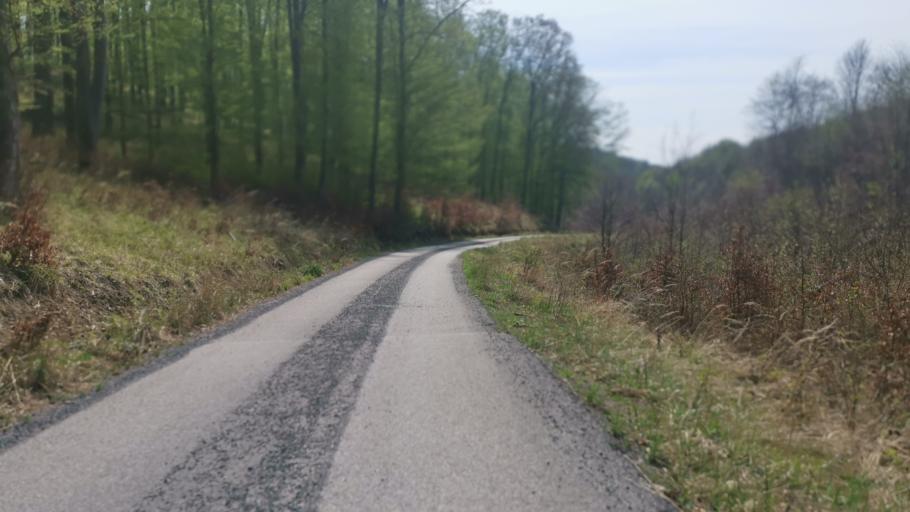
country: SK
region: Nitriansky
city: Brezova pod Bradlom
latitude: 48.5916
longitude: 17.4903
